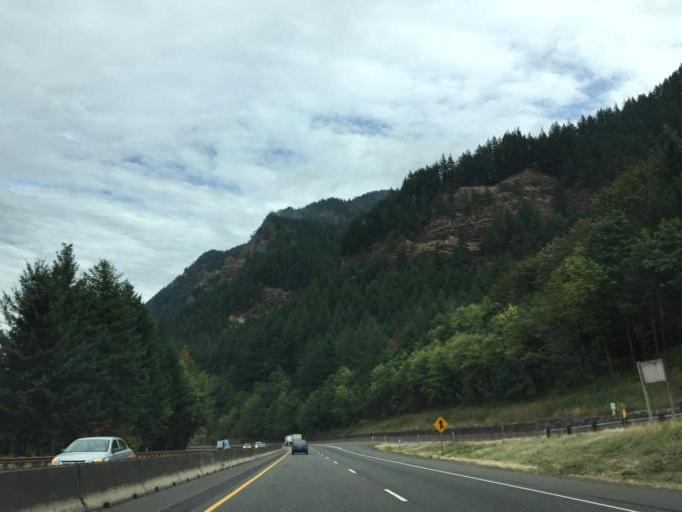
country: US
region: Oregon
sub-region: Hood River County
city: Cascade Locks
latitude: 45.6128
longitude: -122.0046
